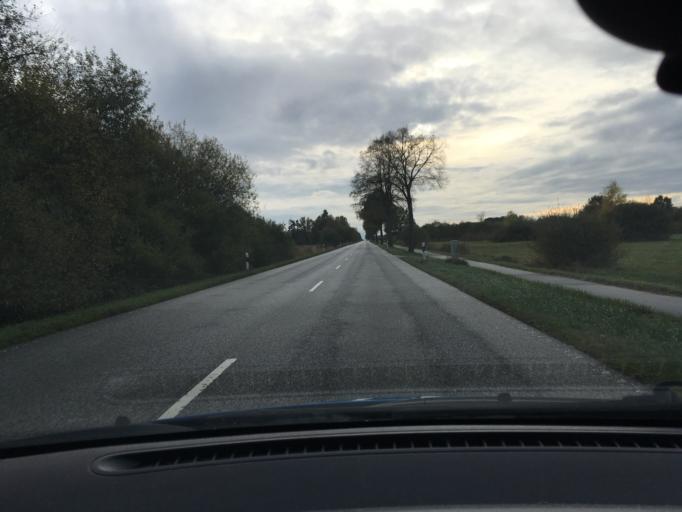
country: DE
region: Schleswig-Holstein
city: Grabau
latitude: 53.5259
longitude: 10.5110
